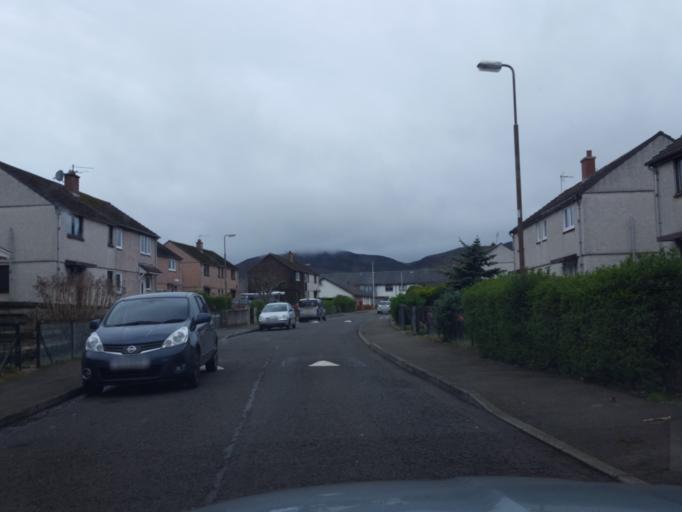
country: GB
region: Scotland
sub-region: Midlothian
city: Penicuik
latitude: 55.8324
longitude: -3.2130
